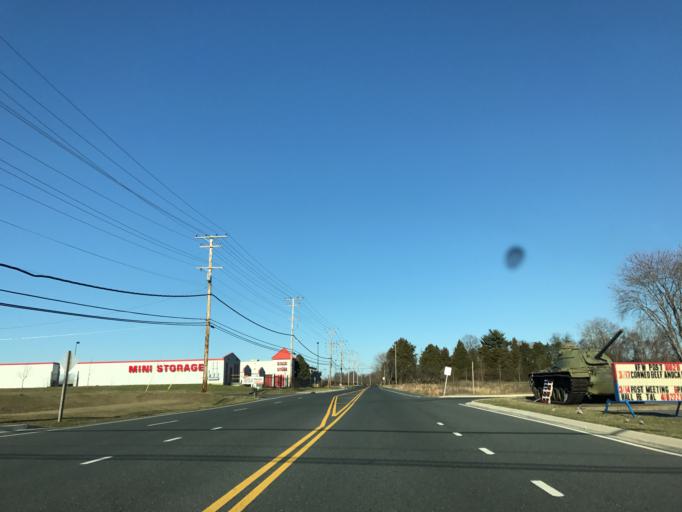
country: US
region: Maryland
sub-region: Harford County
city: Aberdeen
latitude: 39.4929
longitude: -76.1789
